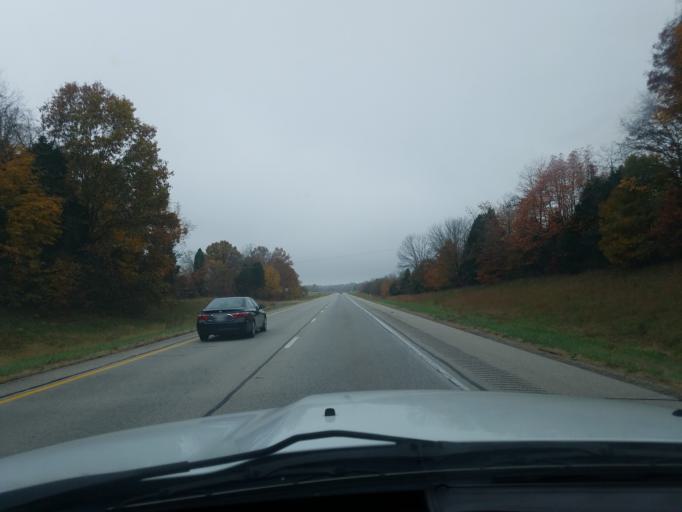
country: US
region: Indiana
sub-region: Harrison County
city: Corydon
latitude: 38.2500
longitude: -86.0588
